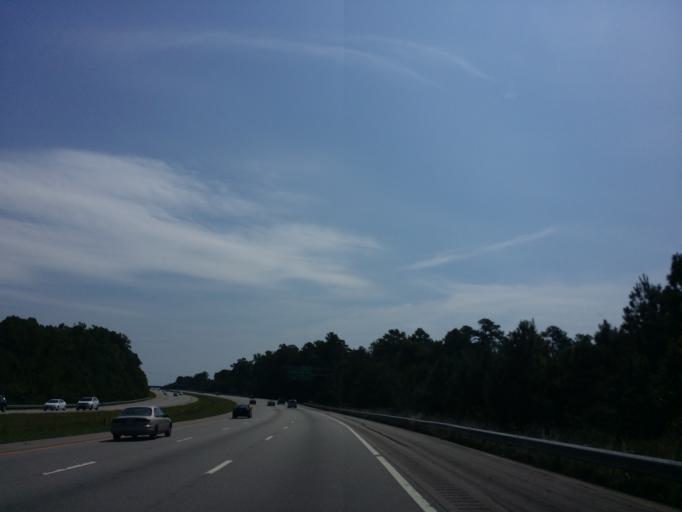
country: US
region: North Carolina
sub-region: Wake County
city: Morrisville
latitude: 35.9089
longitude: -78.7441
